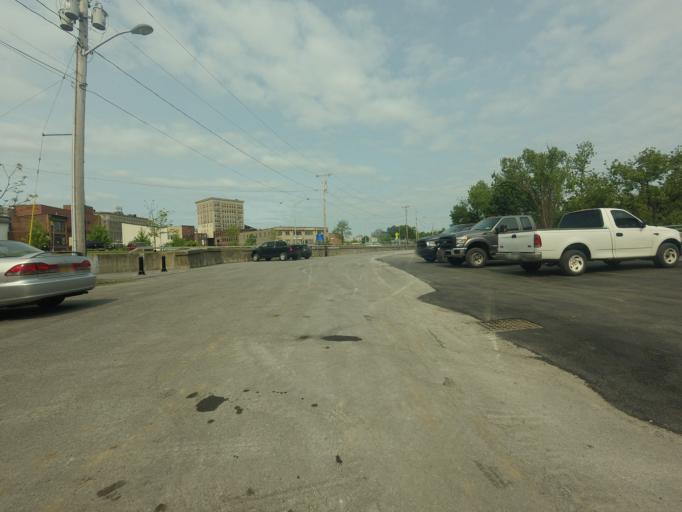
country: US
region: New York
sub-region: Jefferson County
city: Watertown
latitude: 43.9756
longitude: -75.9082
